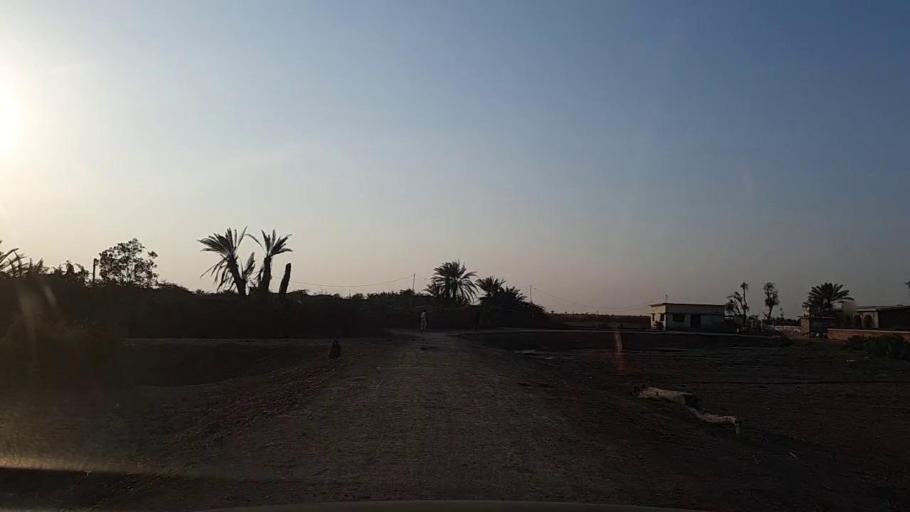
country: PK
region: Sindh
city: Tando Mittha Khan
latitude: 25.9339
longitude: 69.0789
